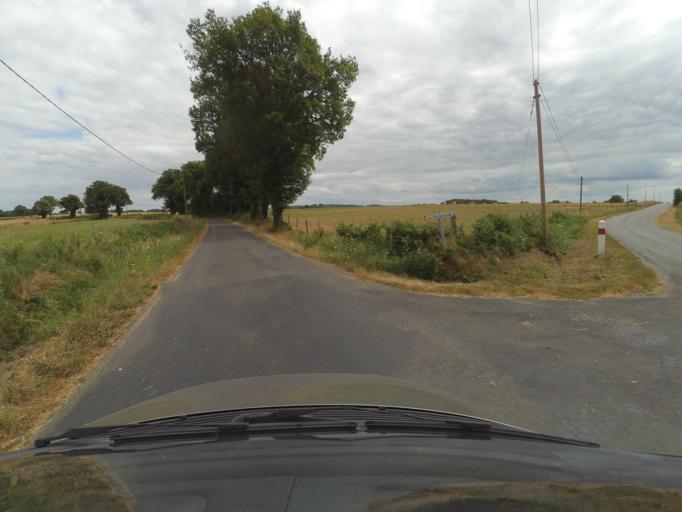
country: FR
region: Limousin
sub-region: Departement de la Haute-Vienne
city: Arnac-la-Poste
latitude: 46.2371
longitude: 1.3327
